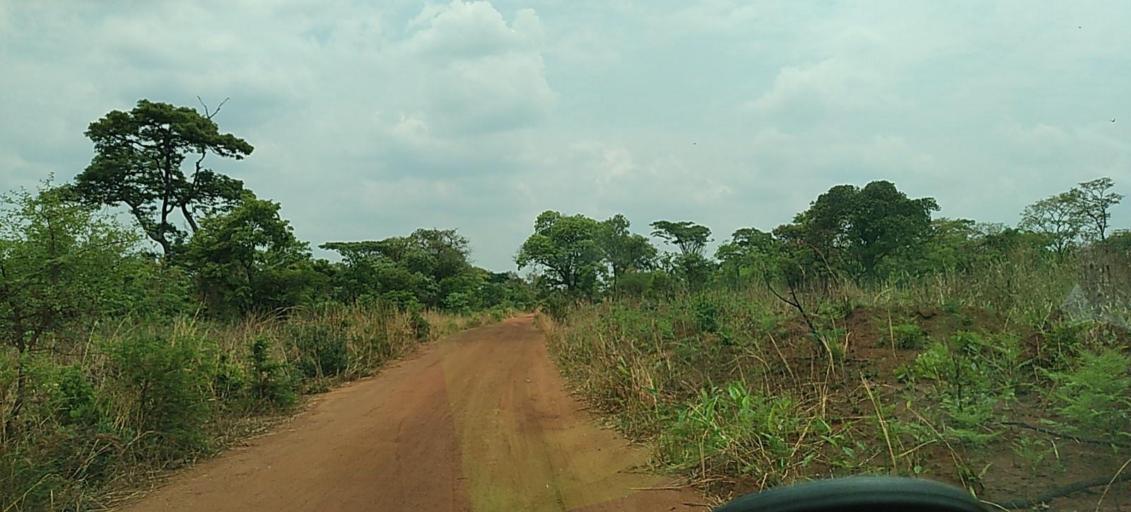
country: ZM
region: North-Western
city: Kansanshi
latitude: -12.0492
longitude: 26.3729
